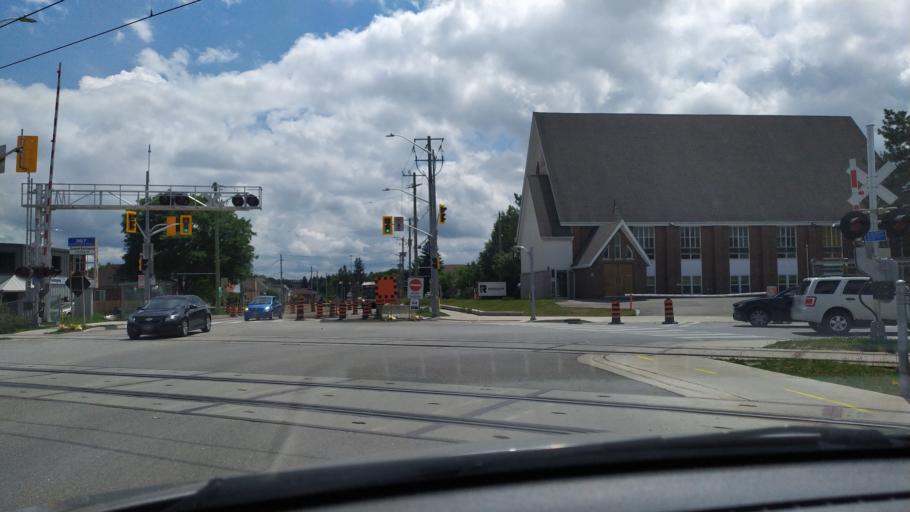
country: CA
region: Ontario
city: Kitchener
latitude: 43.4344
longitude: -80.4787
